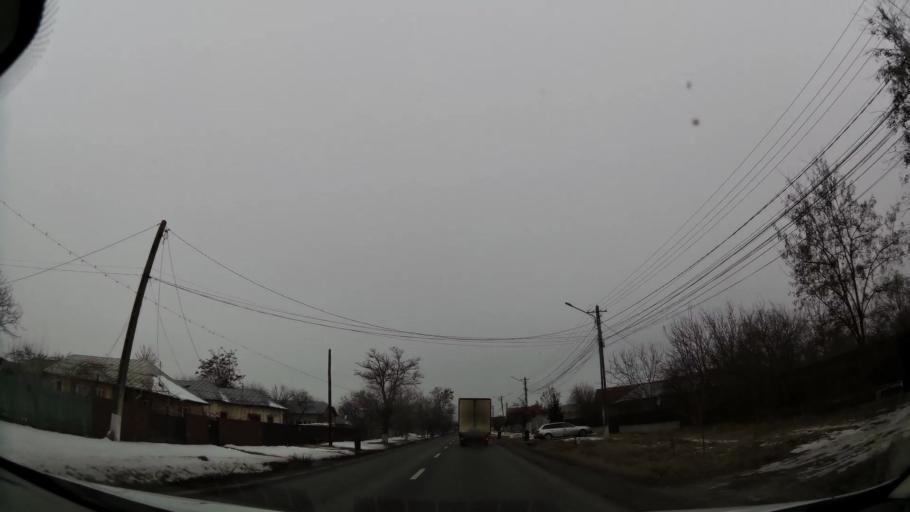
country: RO
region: Dambovita
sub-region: Comuna Tartasesti
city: Baldana
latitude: 44.6188
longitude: 25.7571
